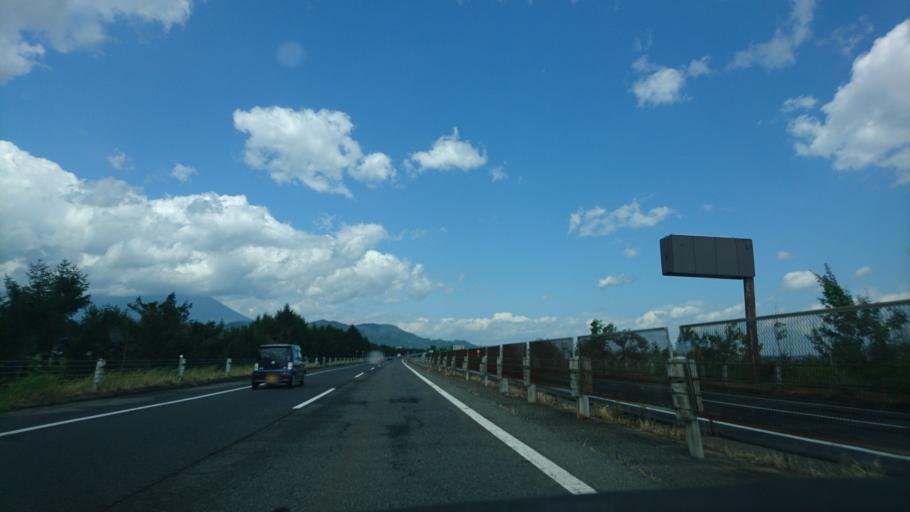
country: JP
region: Iwate
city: Morioka-shi
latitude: 39.7167
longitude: 141.0944
